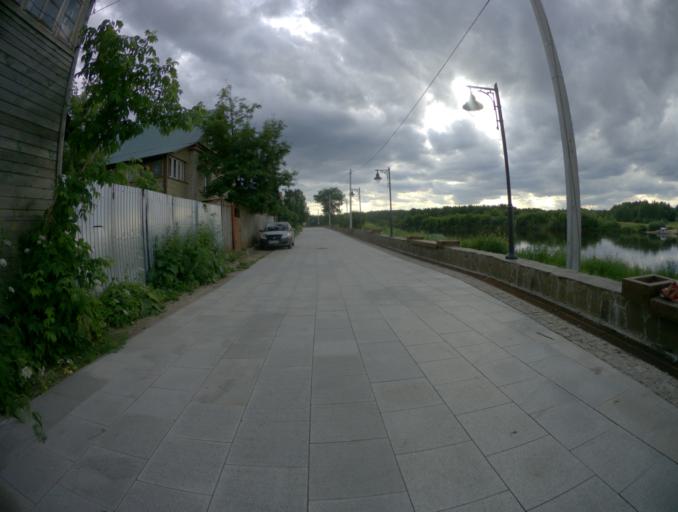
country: RU
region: Vladimir
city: Gorokhovets
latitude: 56.2083
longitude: 42.6783
